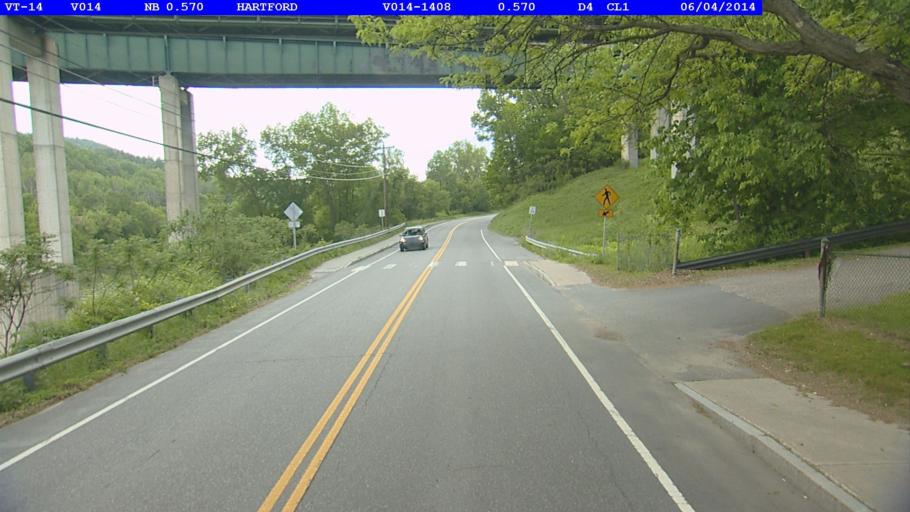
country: US
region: Vermont
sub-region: Windsor County
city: White River Junction
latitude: 43.6557
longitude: -72.3296
